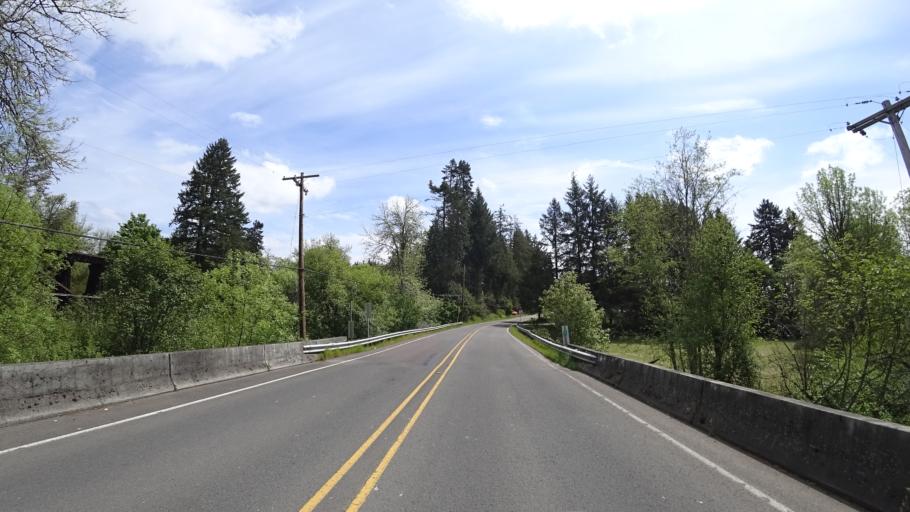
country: US
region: Oregon
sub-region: Washington County
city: Hillsboro
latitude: 45.5426
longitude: -123.0038
